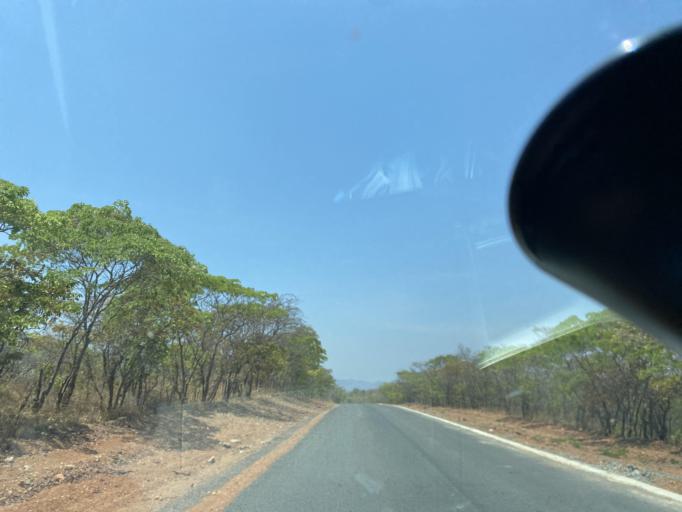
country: ZM
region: Lusaka
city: Kafue
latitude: -15.8620
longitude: 28.4261
